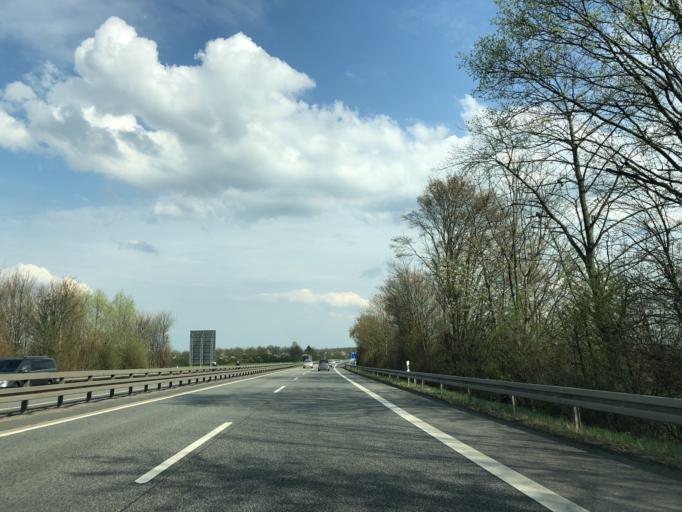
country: DE
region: Hesse
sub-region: Regierungsbezirk Darmstadt
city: Bad Homburg vor der Hoehe
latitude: 50.2101
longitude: 8.6088
